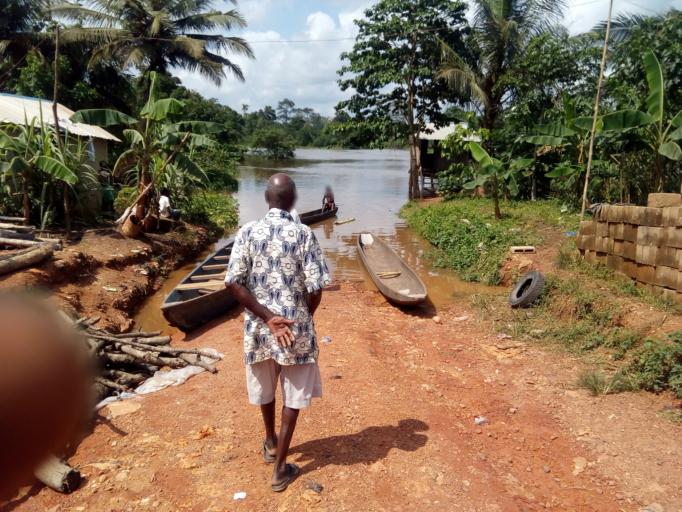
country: CI
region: Sud-Comoe
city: Mafere
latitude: 5.2944
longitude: -2.7847
